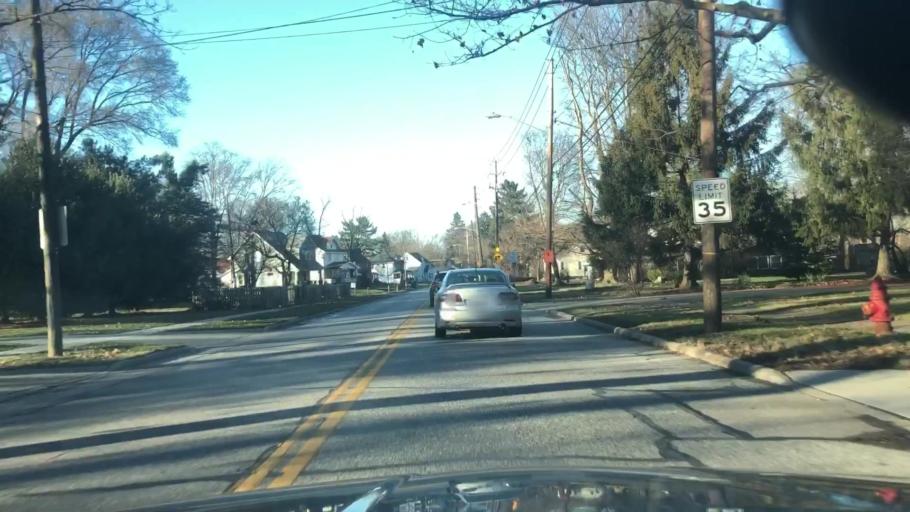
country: US
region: Ohio
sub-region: Cuyahoga County
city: Berea
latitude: 41.3581
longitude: -81.8603
